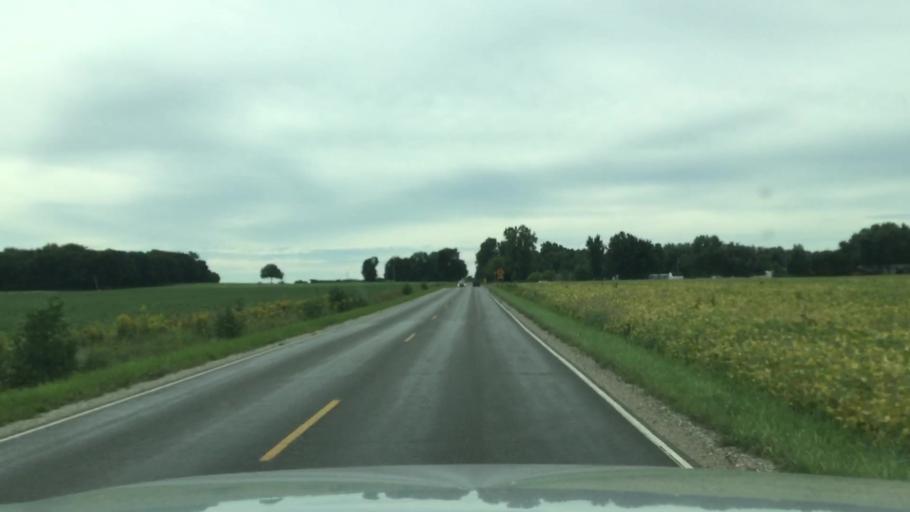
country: US
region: Michigan
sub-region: Shiawassee County
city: Durand
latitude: 42.9882
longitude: -83.9868
